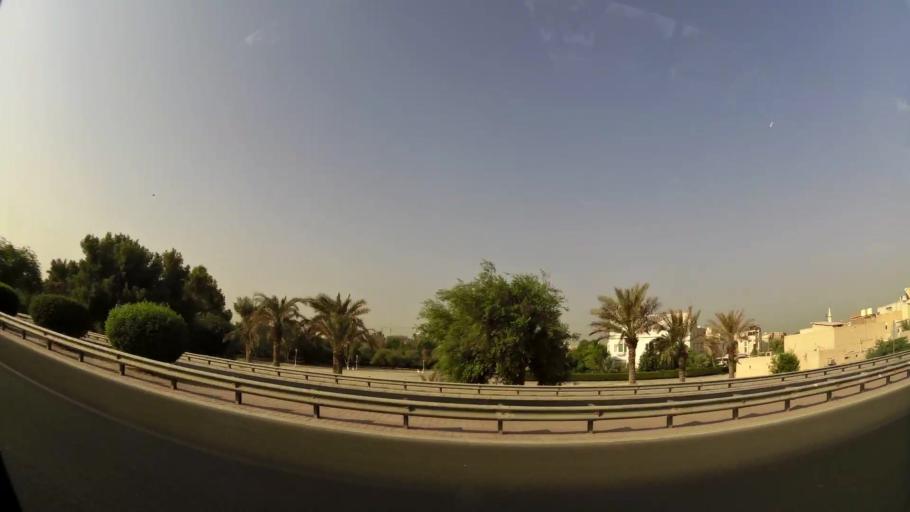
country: KW
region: Muhafazat Hawalli
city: Hawalli
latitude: 29.3457
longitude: 48.0314
